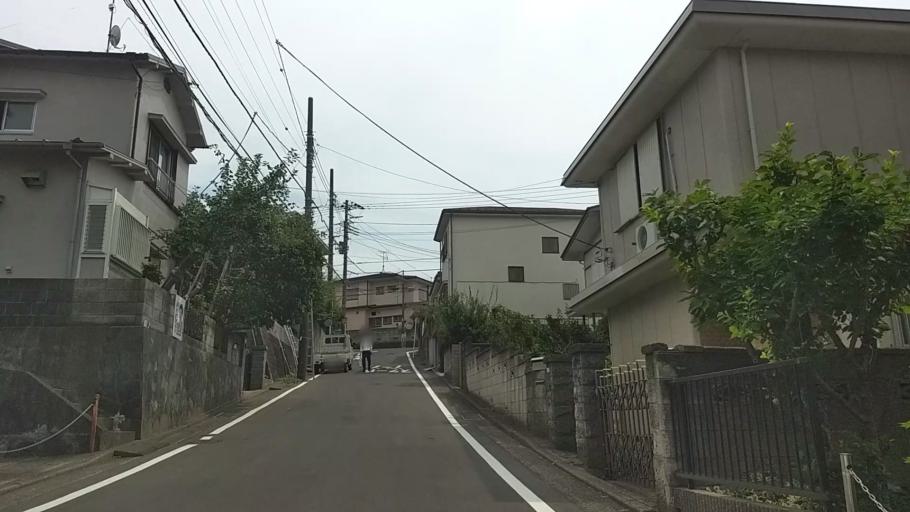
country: JP
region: Kanagawa
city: Yokohama
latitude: 35.4405
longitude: 139.6012
